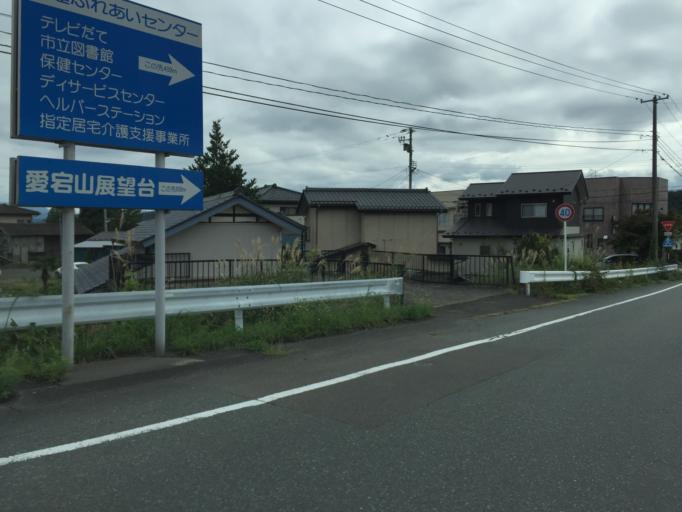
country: JP
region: Fukushima
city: Hobaramachi
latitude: 37.8198
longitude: 140.5124
